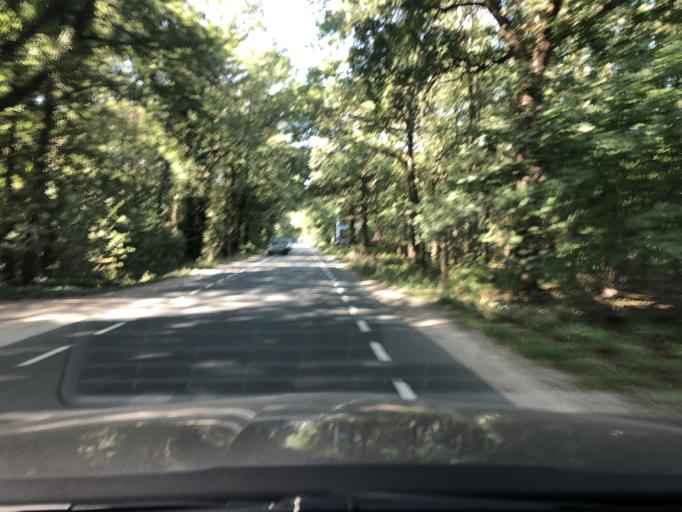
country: NL
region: North Brabant
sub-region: Gemeente Haaren
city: Haaren
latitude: 51.6701
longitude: 5.2034
